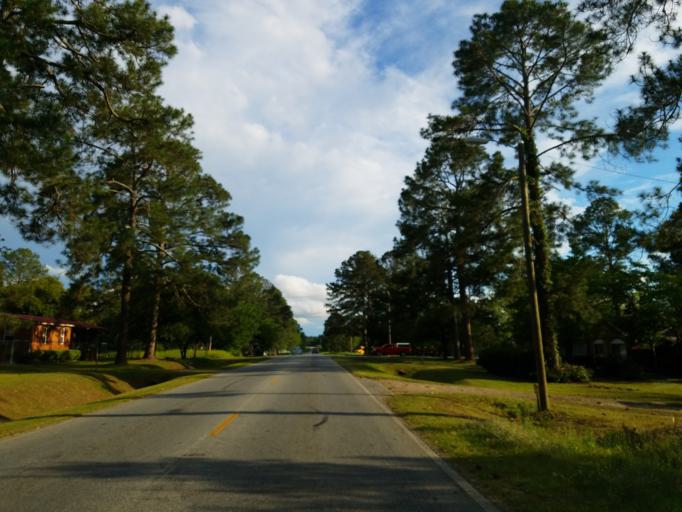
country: US
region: Georgia
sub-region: Crisp County
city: Cordele
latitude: 31.9499
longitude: -83.7877
